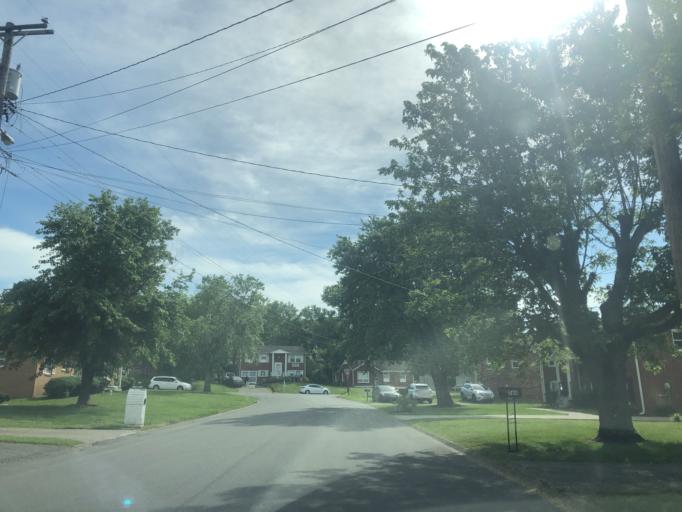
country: US
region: Tennessee
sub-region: Davidson County
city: Nashville
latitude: 36.2161
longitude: -86.8163
